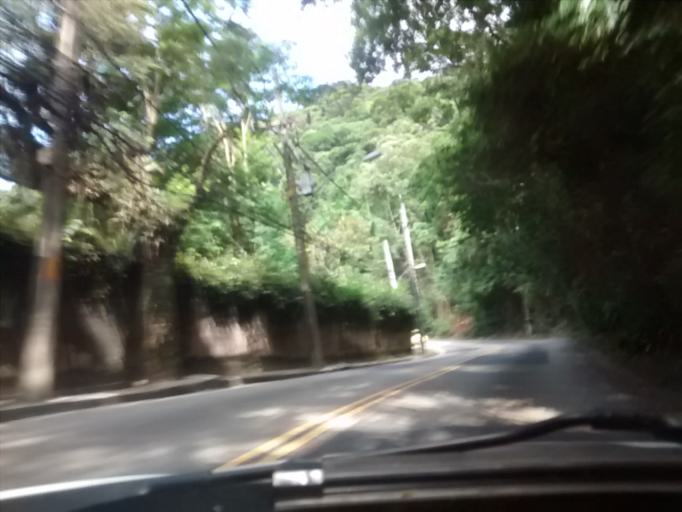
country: BR
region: Rio de Janeiro
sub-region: Rio De Janeiro
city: Rio de Janeiro
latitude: -22.9697
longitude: -43.2803
